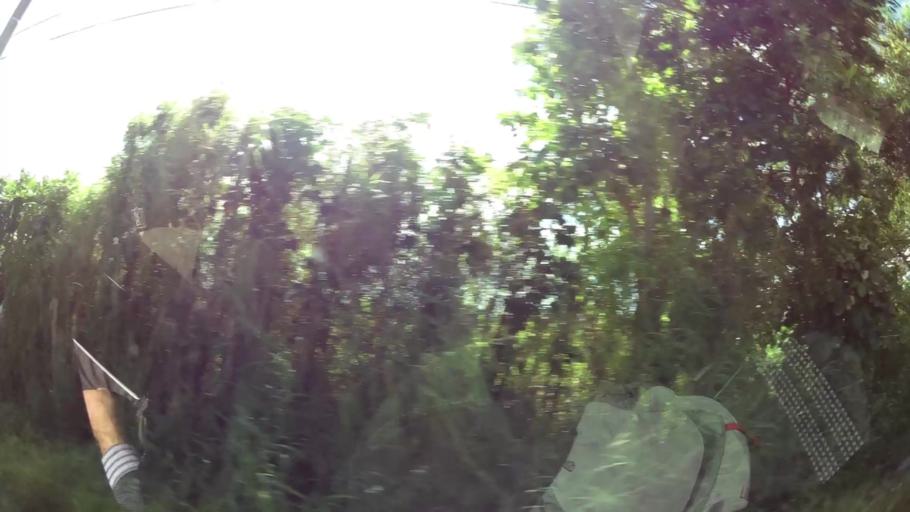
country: GP
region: Guadeloupe
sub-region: Guadeloupe
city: Le Moule
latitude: 16.3476
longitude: -61.4147
